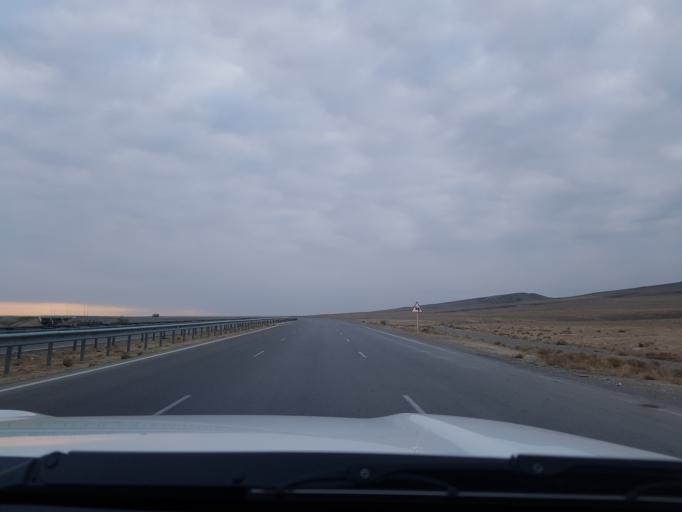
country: IR
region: Razavi Khorasan
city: Dargaz
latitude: 37.6835
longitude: 59.0712
